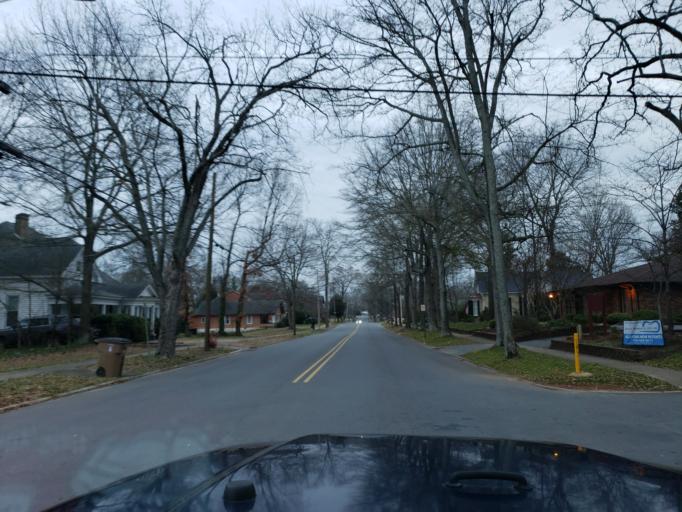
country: US
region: North Carolina
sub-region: Cleveland County
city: Shelby
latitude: 35.2982
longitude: -81.5416
